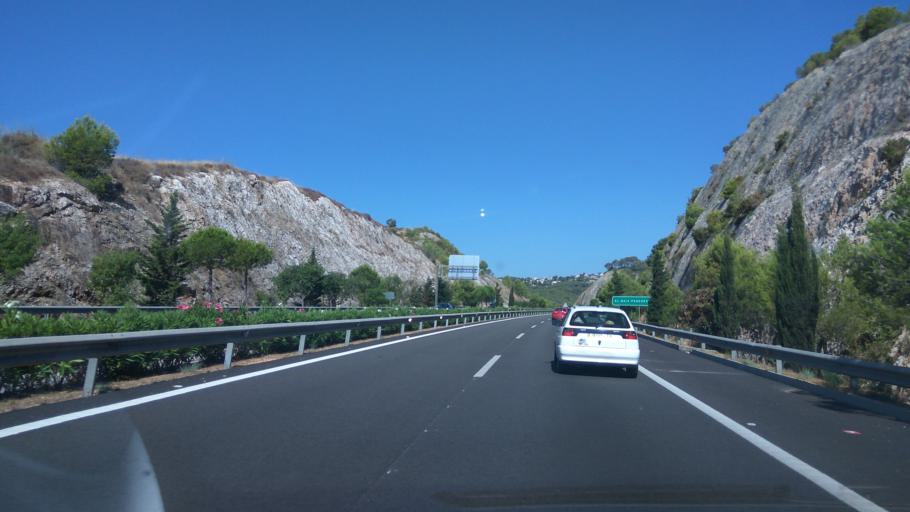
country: ES
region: Catalonia
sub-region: Provincia de Tarragona
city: Cunit
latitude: 41.2103
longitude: 1.6422
